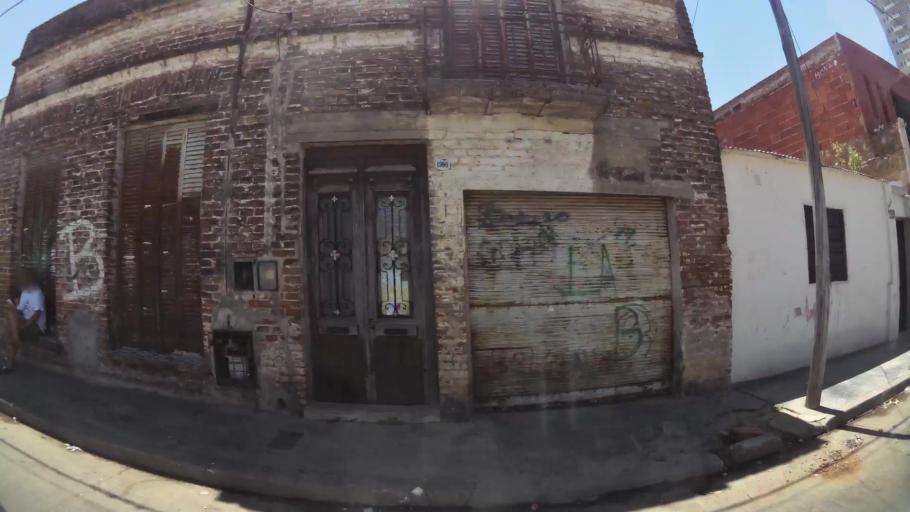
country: AR
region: Cordoba
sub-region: Departamento de Capital
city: Cordoba
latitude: -31.4011
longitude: -64.2069
